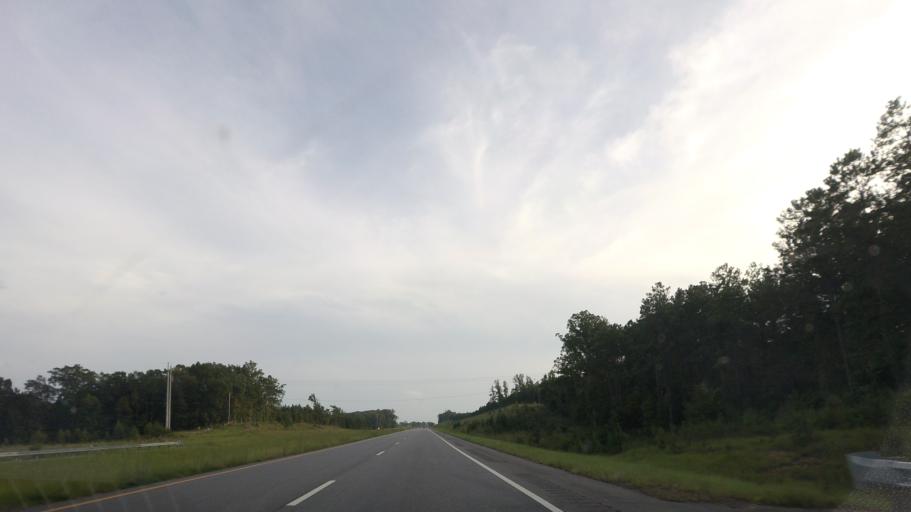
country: US
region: Georgia
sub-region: Wilkinson County
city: Gordon
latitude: 32.8687
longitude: -83.3767
